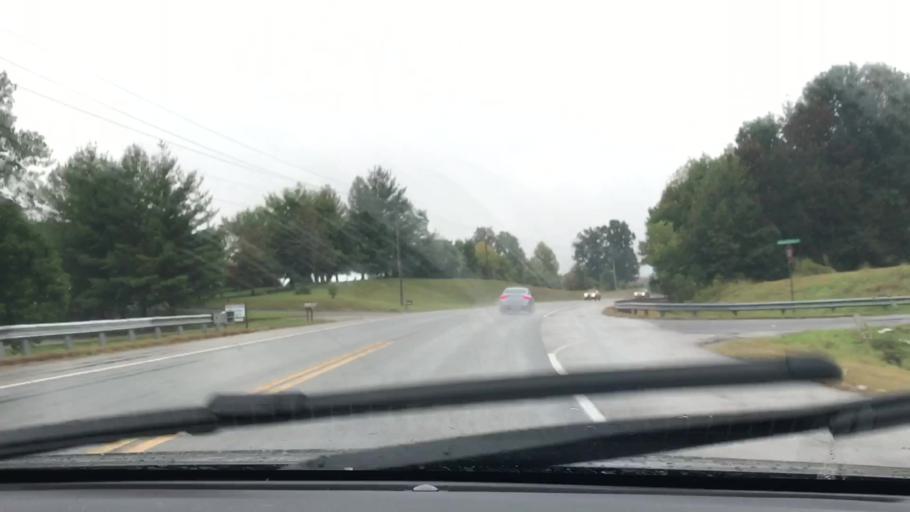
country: US
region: Tennessee
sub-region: Sumner County
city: Westmoreland
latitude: 36.5286
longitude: -86.1788
